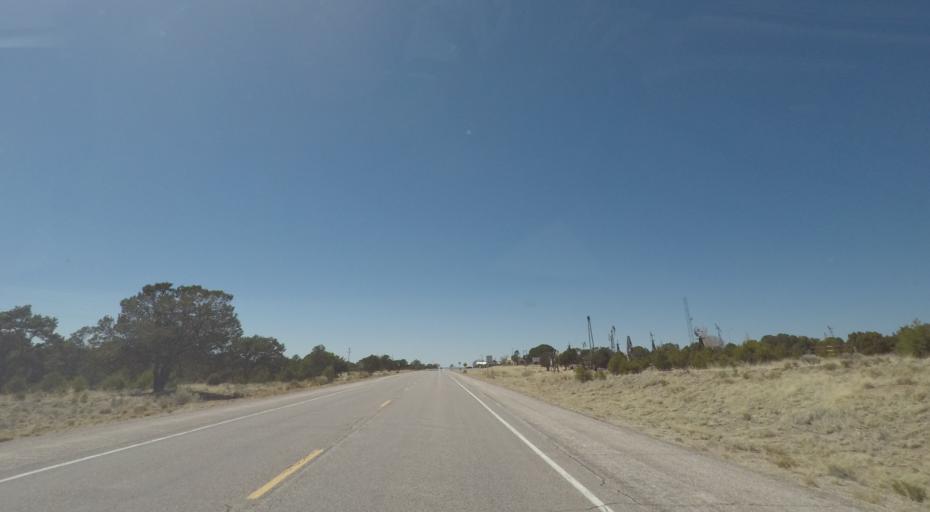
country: US
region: New Mexico
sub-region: Socorro County
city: Alamo
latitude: 34.2975
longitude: -108.1255
